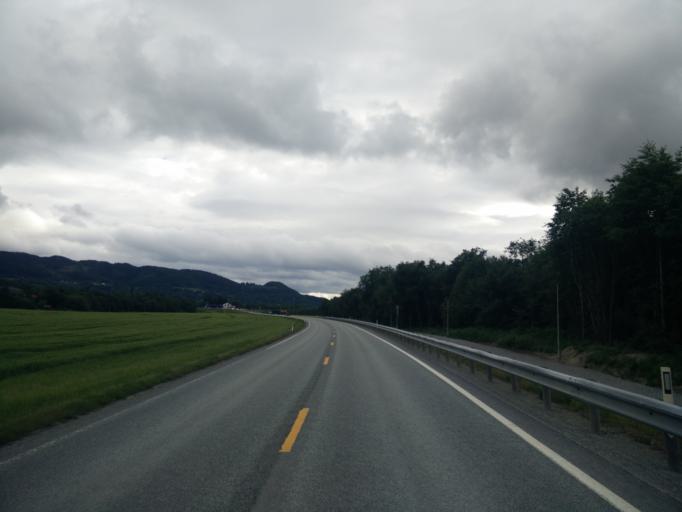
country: NO
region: Sor-Trondelag
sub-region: Orkdal
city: Orkanger
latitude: 63.2721
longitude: 9.8054
